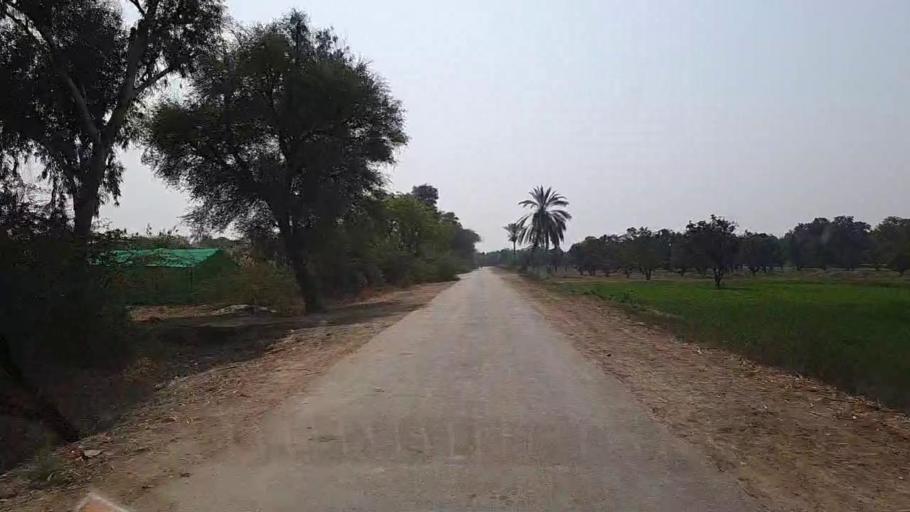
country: PK
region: Sindh
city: Mirwah Gorchani
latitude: 25.3219
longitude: 69.0024
